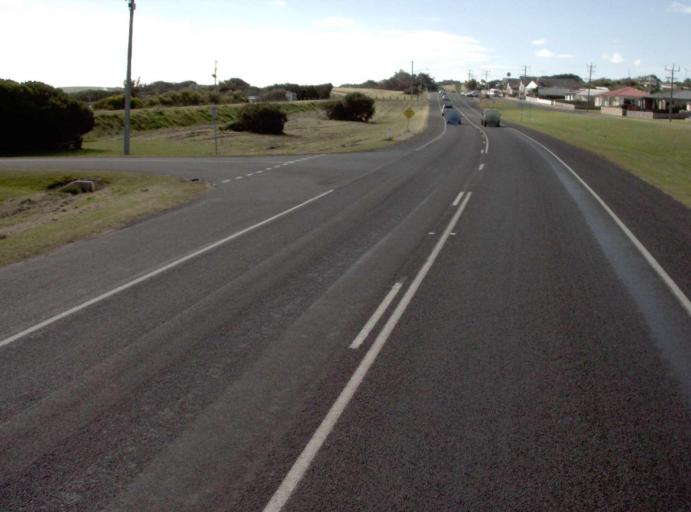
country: AU
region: Victoria
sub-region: Bass Coast
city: North Wonthaggi
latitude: -38.5516
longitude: 145.4788
